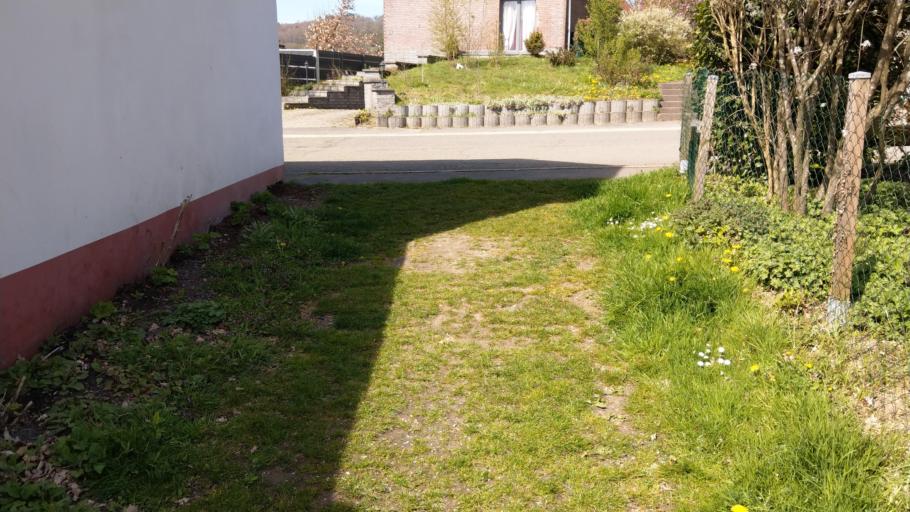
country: BE
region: Wallonia
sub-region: Province de Liege
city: La Calamine
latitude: 50.7425
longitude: 5.9973
